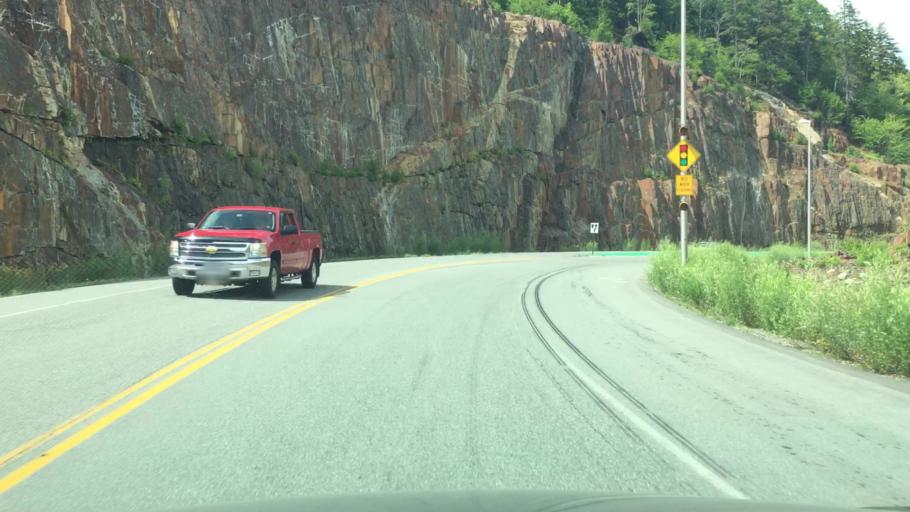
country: US
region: Maine
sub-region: Hancock County
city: Bucksport
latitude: 44.5599
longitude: -68.8072
